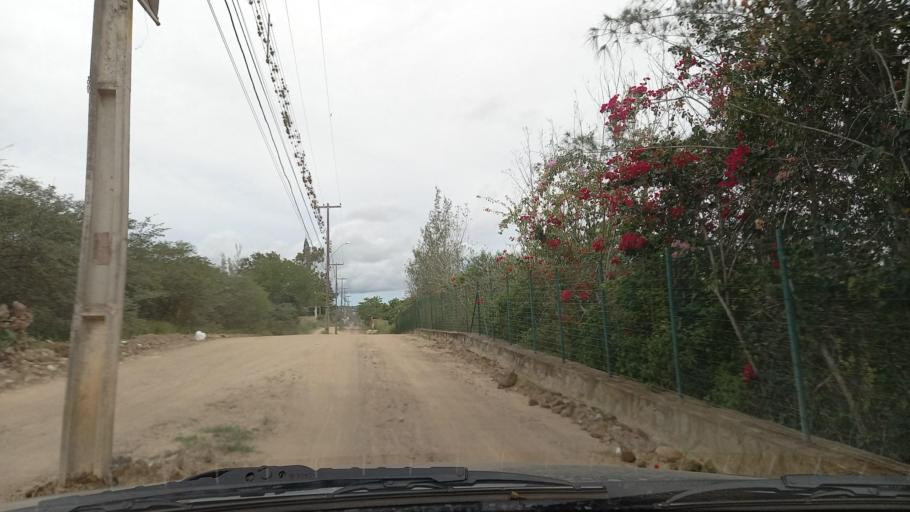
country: BR
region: Pernambuco
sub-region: Gravata
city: Gravata
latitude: -8.1969
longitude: -35.6003
